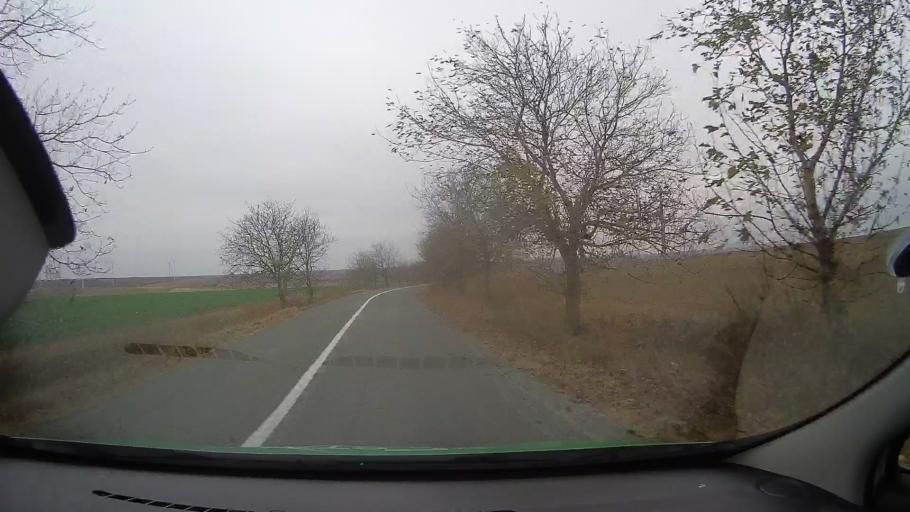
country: RO
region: Constanta
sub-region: Comuna Targusor
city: Targusor
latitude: 44.4823
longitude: 28.3708
